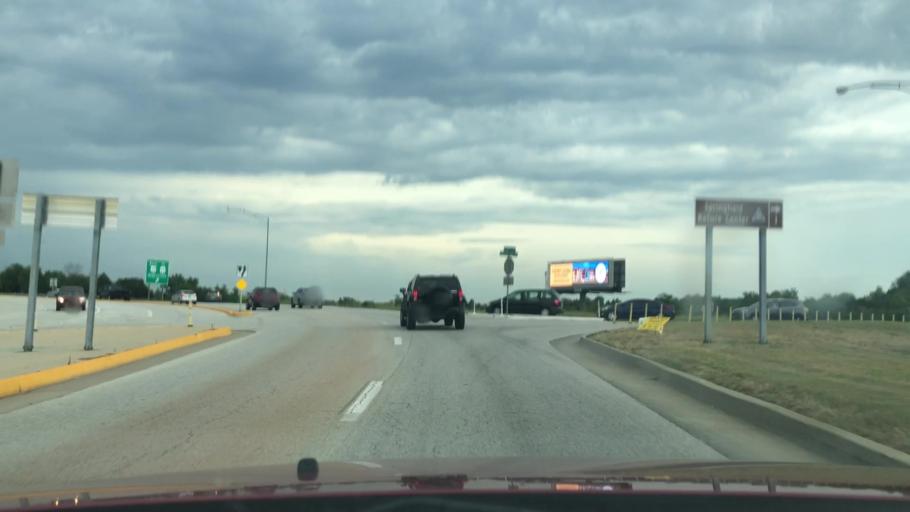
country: US
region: Missouri
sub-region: Greene County
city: Springfield
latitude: 37.1373
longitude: -93.2537
